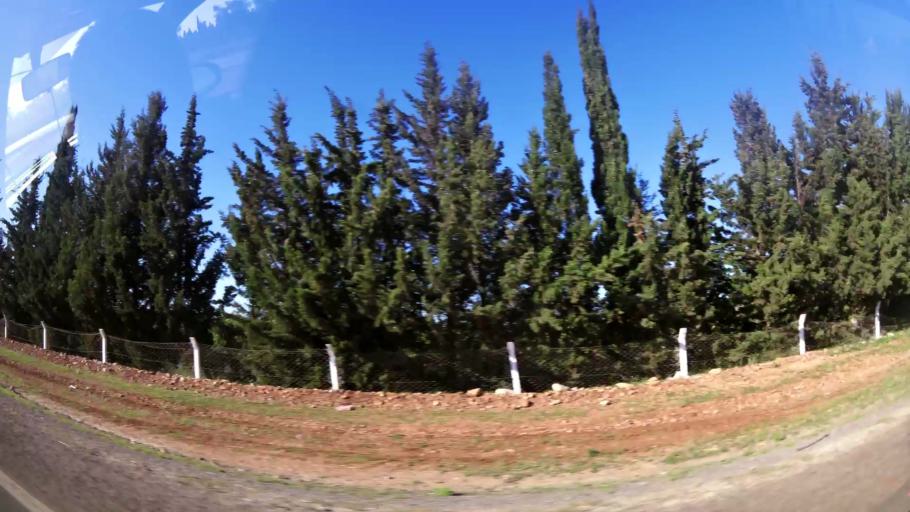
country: MA
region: Oriental
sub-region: Berkane-Taourirt
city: Ahfir
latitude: 35.0014
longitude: -2.1770
